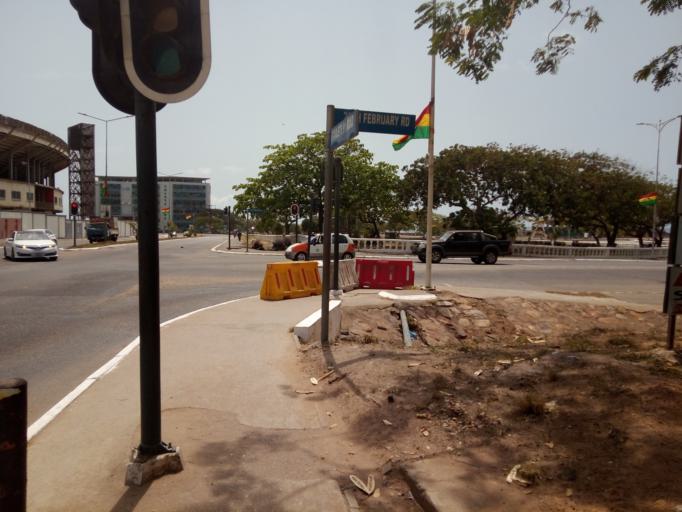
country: GH
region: Greater Accra
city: Accra
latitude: 5.5505
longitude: -0.1931
